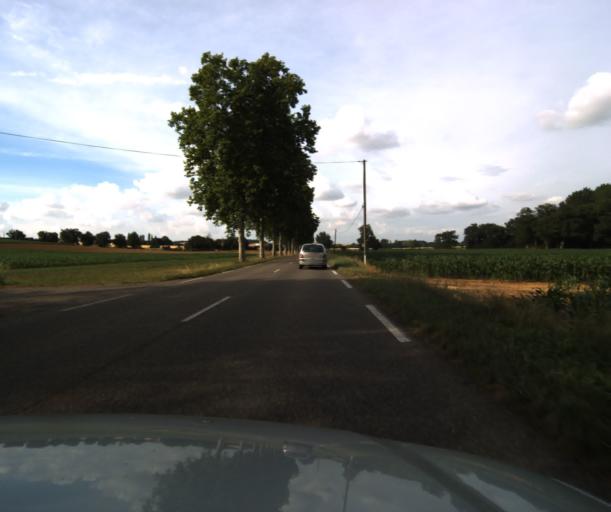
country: FR
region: Midi-Pyrenees
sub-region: Departement du Tarn-et-Garonne
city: Beaumont-de-Lomagne
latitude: 43.8342
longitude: 0.9239
